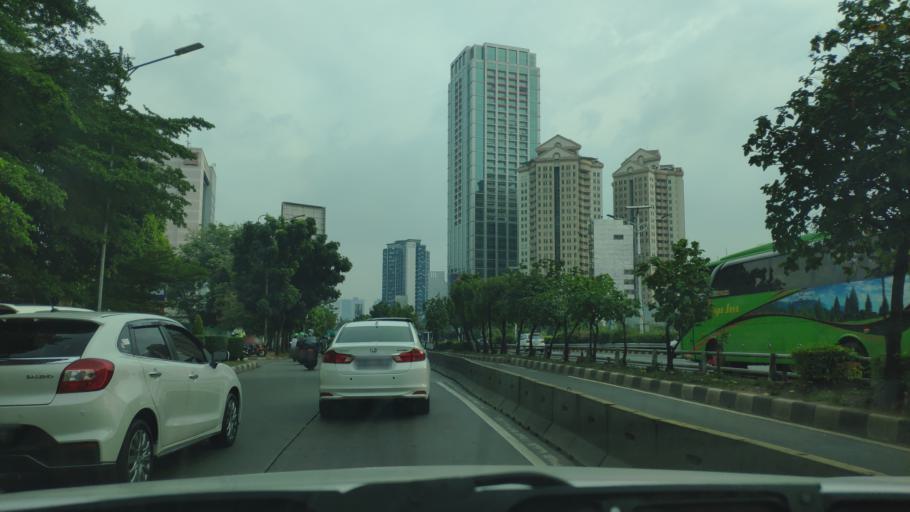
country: ID
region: Jakarta Raya
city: Jakarta
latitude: -6.1975
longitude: 106.7981
